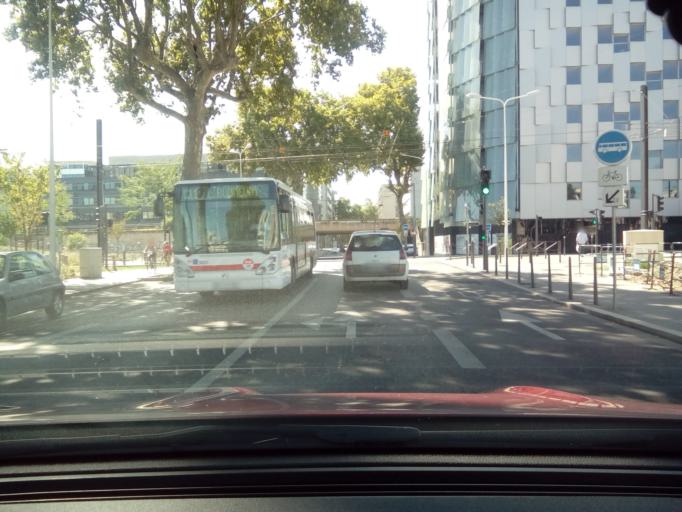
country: FR
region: Rhone-Alpes
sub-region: Departement du Rhone
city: Lyon
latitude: 45.7541
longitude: 4.8624
